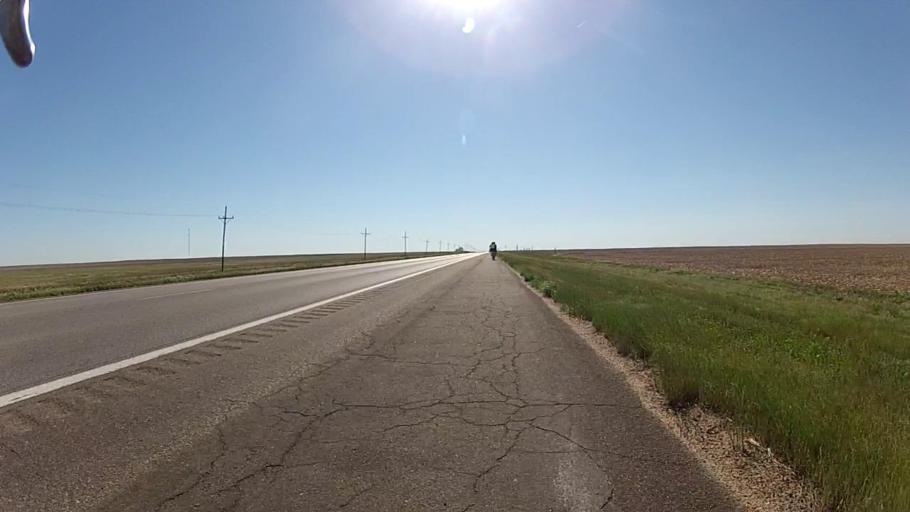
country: US
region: Kansas
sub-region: Kiowa County
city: Greensburg
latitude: 37.5863
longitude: -99.6233
